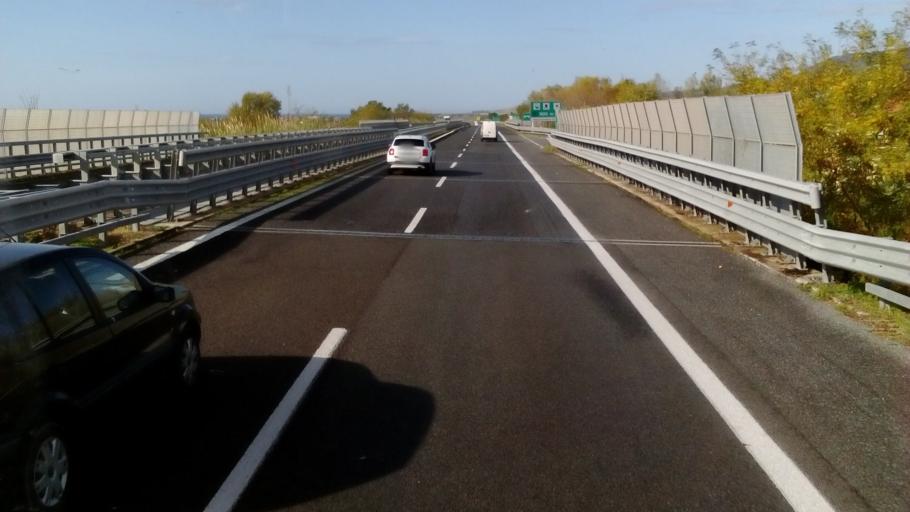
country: IT
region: Calabria
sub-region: Provincia di Catanzaro
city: Santa Eufemia Lamezia
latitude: 38.9274
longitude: 16.2458
